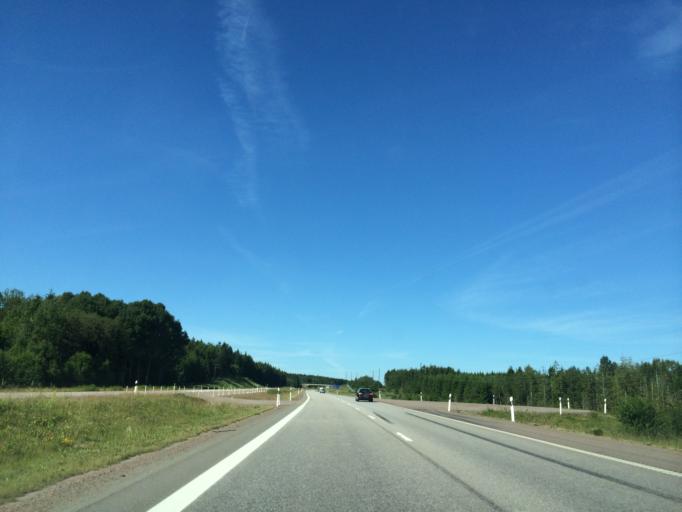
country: SE
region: OEstergoetland
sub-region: Boxholms Kommun
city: Boxholm
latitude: 58.2993
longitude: 14.9380
